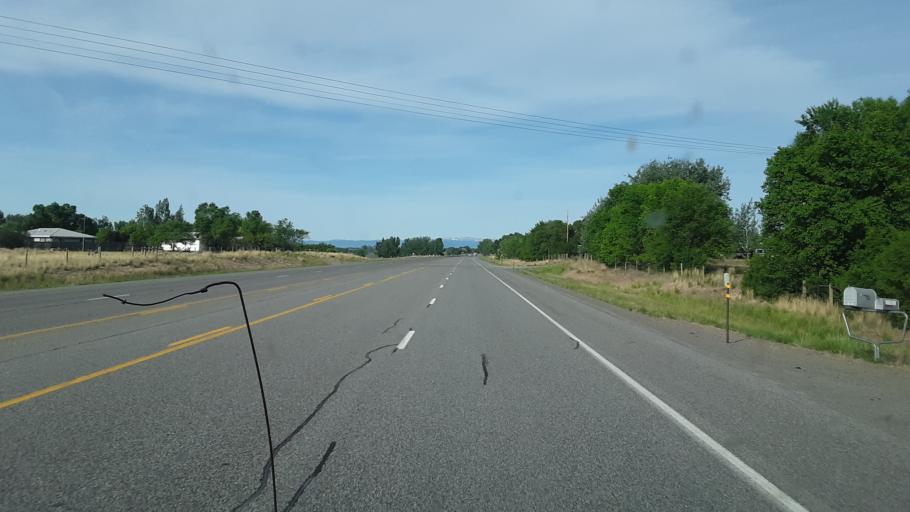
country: US
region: Wyoming
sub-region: Fremont County
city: Riverton
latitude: 43.0995
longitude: -108.3559
